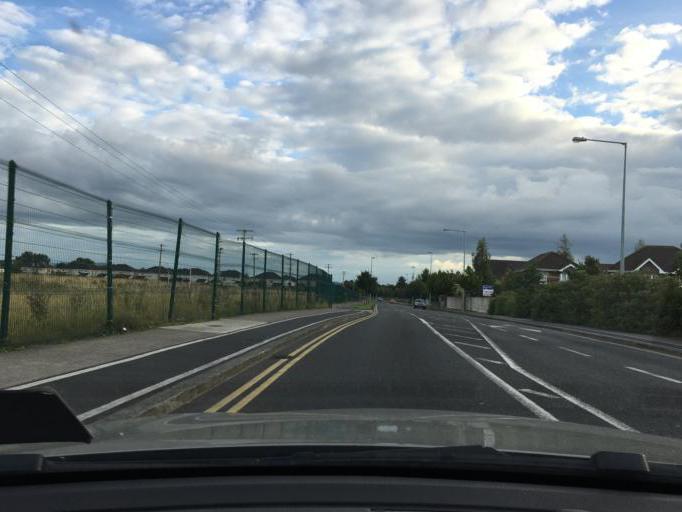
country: IE
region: Leinster
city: Hartstown
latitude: 53.3882
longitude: -6.4183
